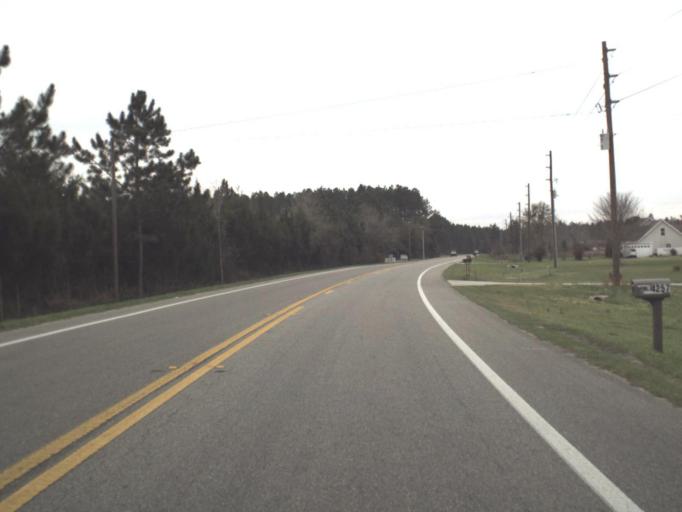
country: US
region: Florida
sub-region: Gulf County
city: Wewahitchka
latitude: 30.1774
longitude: -85.2049
